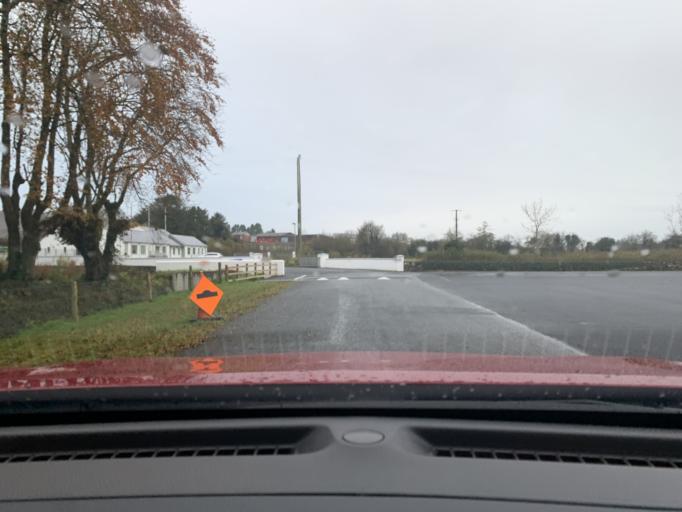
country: IE
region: Connaught
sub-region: Sligo
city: Ballymote
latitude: 53.9950
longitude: -8.5143
